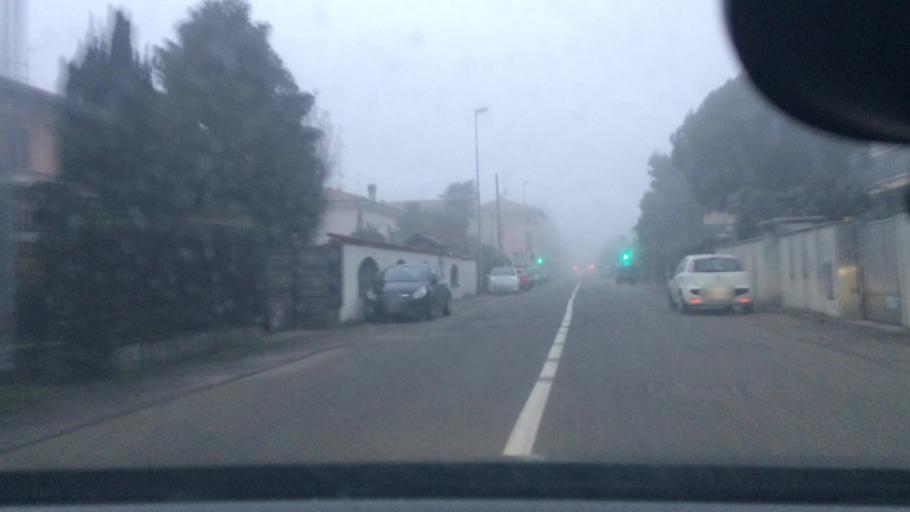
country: IT
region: Lombardy
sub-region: Citta metropolitana di Milano
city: Nerviano
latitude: 45.5483
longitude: 8.9721
